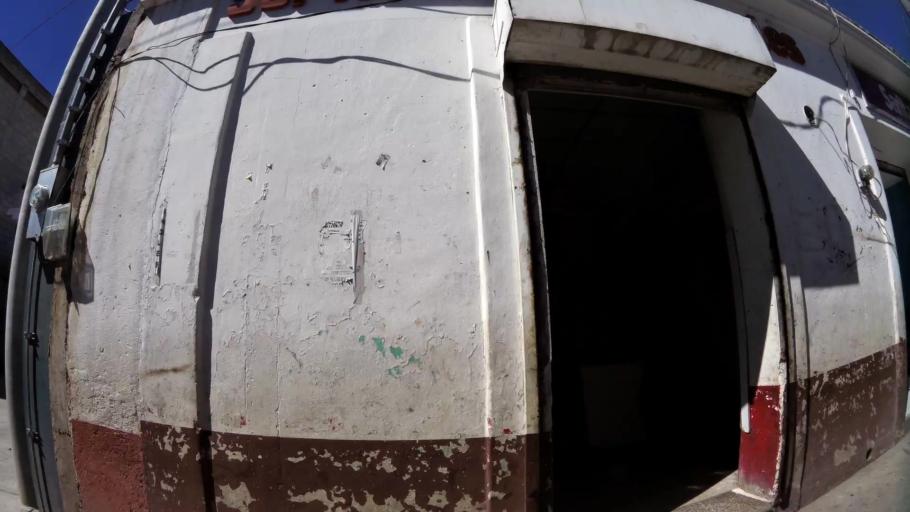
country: GT
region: Solola
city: Solola
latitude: 14.7712
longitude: -91.1827
